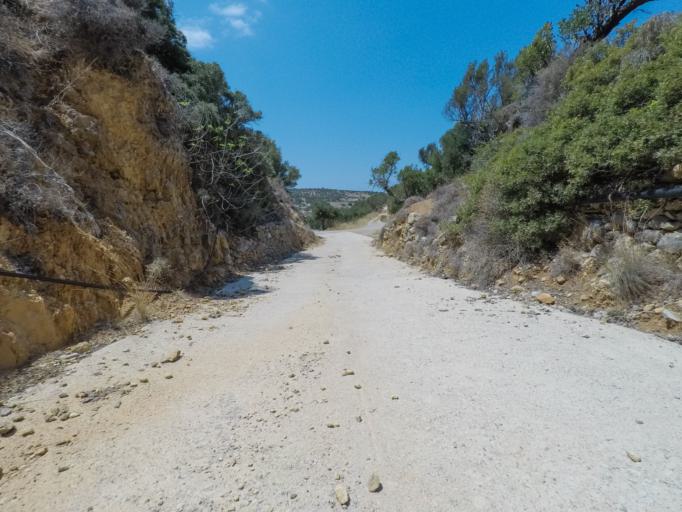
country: GR
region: Crete
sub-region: Nomos Lasithiou
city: Elounda
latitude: 35.3151
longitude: 25.7373
